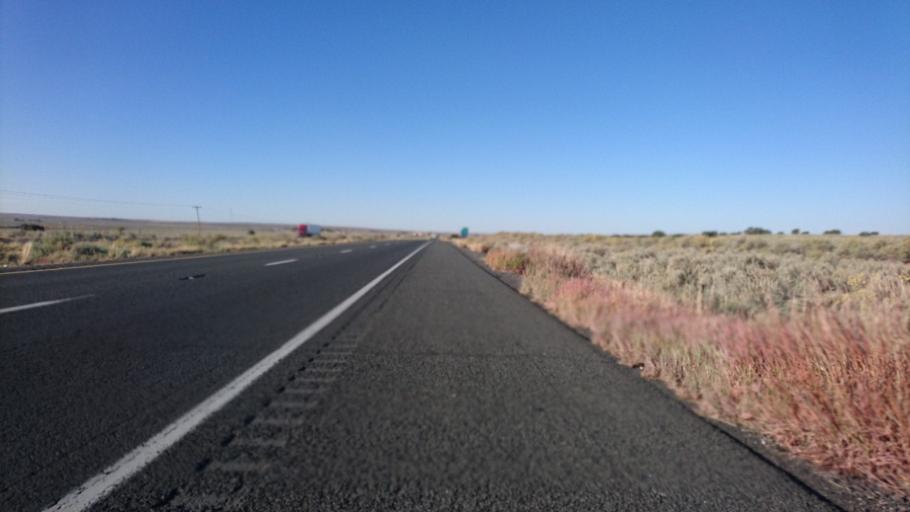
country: US
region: Arizona
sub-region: Apache County
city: Houck
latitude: 35.1398
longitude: -109.5245
